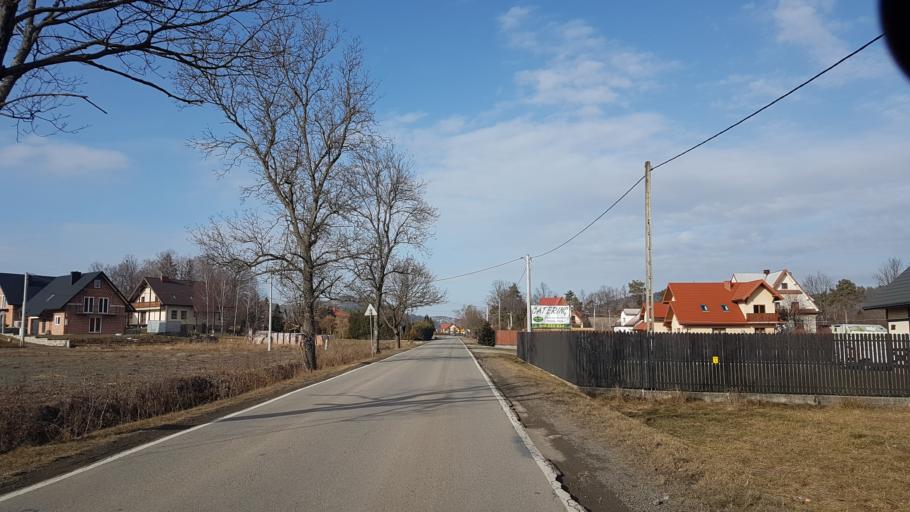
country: PL
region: Lesser Poland Voivodeship
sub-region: Powiat limanowski
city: Lukowica
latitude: 49.6534
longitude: 20.4961
